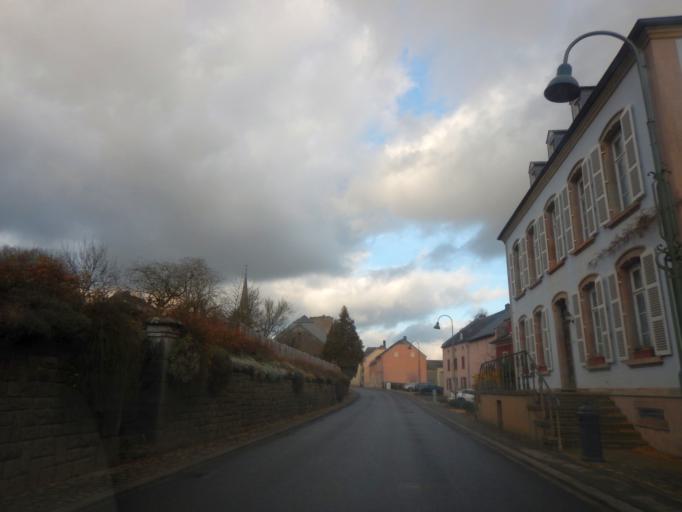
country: LU
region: Diekirch
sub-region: Canton de Redange
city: Useldange
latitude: 49.7659
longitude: 5.9791
